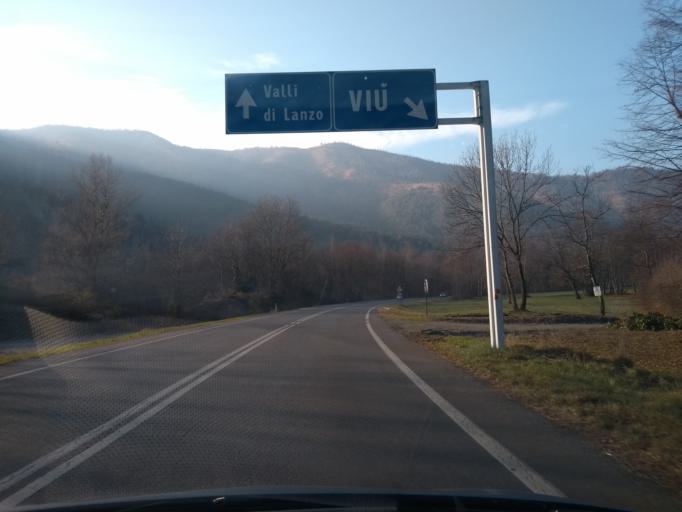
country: IT
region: Piedmont
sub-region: Provincia di Torino
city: Germagnano
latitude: 45.2582
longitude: 7.4696
